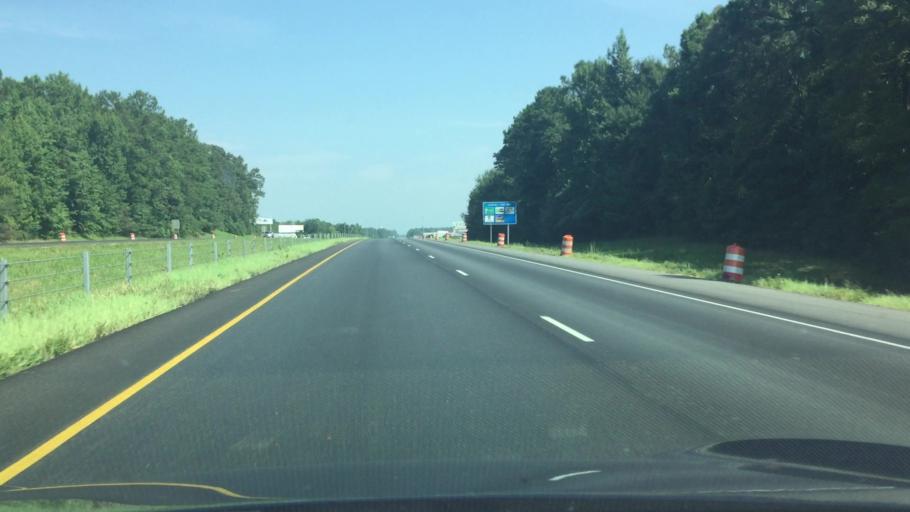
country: US
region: Alabama
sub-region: Chilton County
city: Clanton
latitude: 32.7915
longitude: -86.5763
